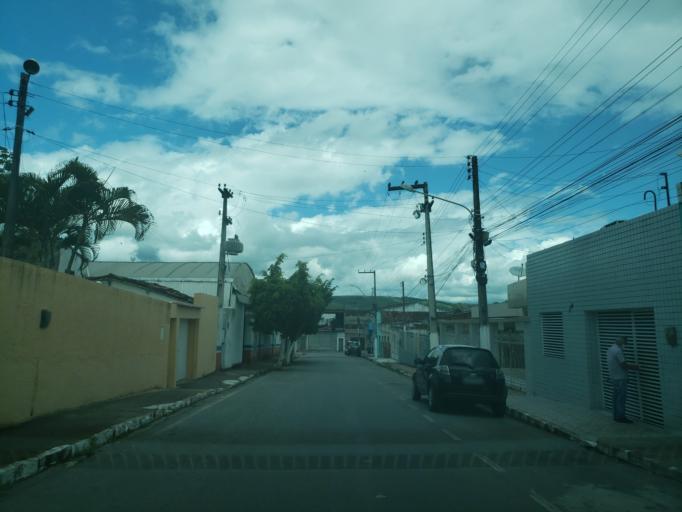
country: BR
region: Alagoas
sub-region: Uniao Dos Palmares
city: Uniao dos Palmares
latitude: -9.1587
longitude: -36.0310
